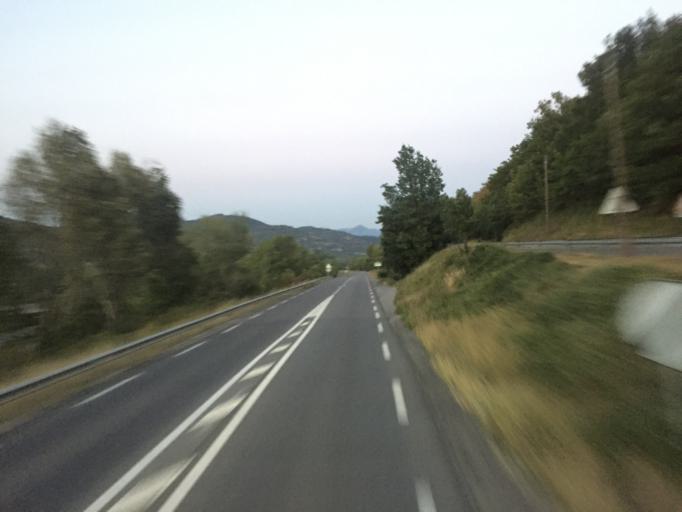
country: FR
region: Provence-Alpes-Cote d'Azur
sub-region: Departement des Alpes-de-Haute-Provence
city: Malijai
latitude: 44.0421
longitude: 6.0337
